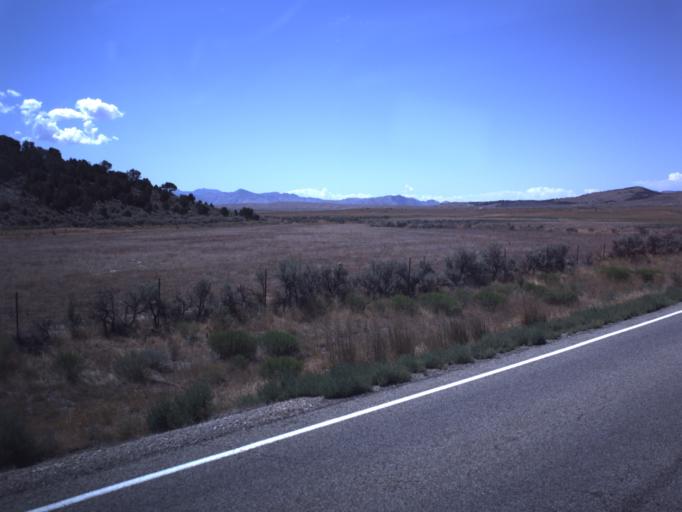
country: US
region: Utah
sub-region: Juab County
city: Nephi
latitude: 39.6968
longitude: -111.9875
